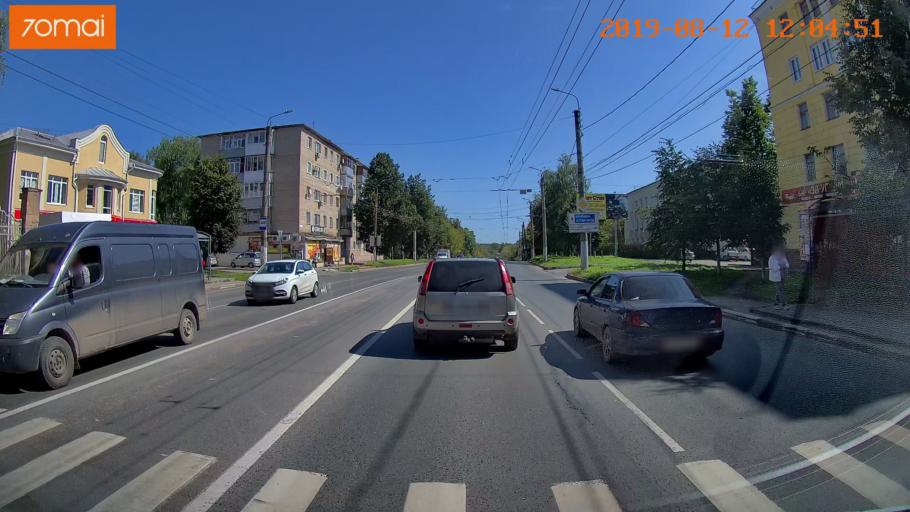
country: RU
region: Ivanovo
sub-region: Gorod Ivanovo
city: Ivanovo
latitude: 56.9944
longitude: 41.0059
